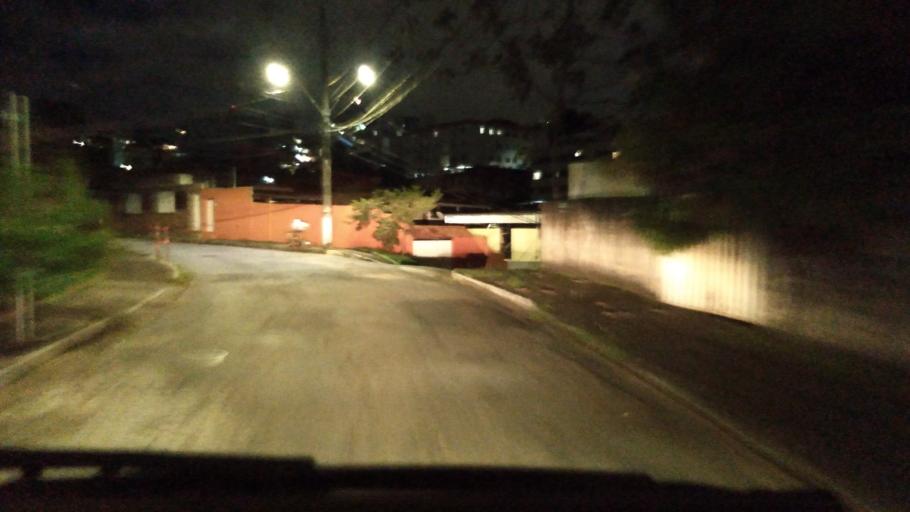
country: BR
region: Minas Gerais
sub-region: Belo Horizonte
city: Belo Horizonte
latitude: -19.8975
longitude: -43.9756
